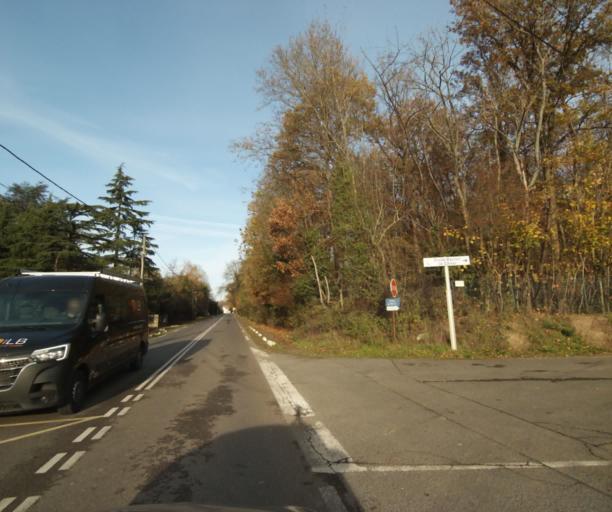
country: FR
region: Ile-de-France
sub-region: Departement des Yvelines
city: Triel-sur-Seine
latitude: 48.9993
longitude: 2.0095
